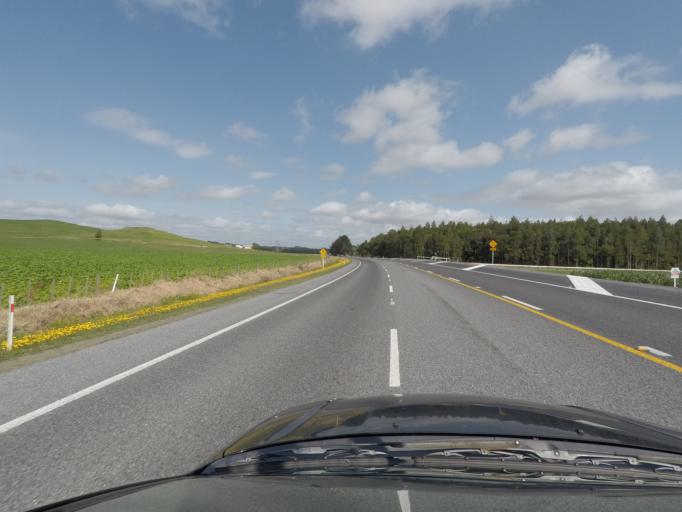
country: NZ
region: Northland
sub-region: Whangarei
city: Ruakaka
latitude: -35.8822
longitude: 174.4207
